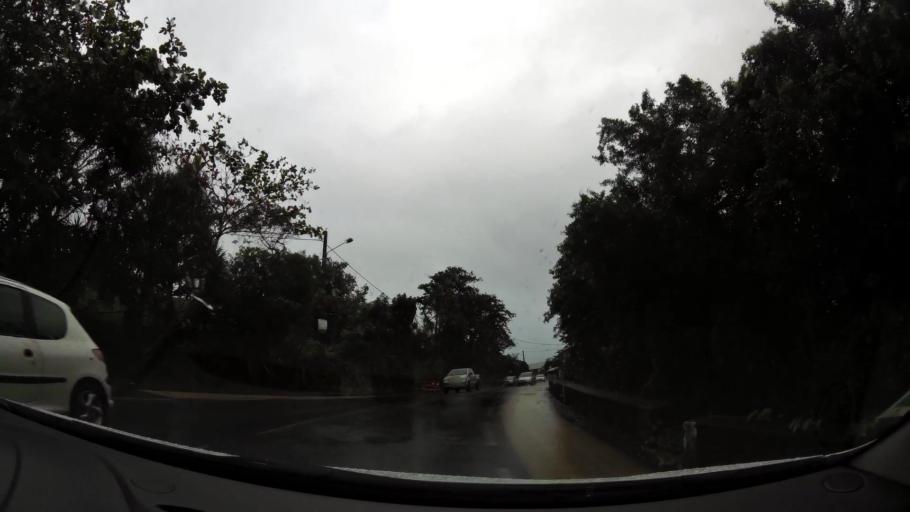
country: RE
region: Reunion
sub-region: Reunion
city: Saint-Benoit
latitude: -21.0216
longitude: 55.7025
